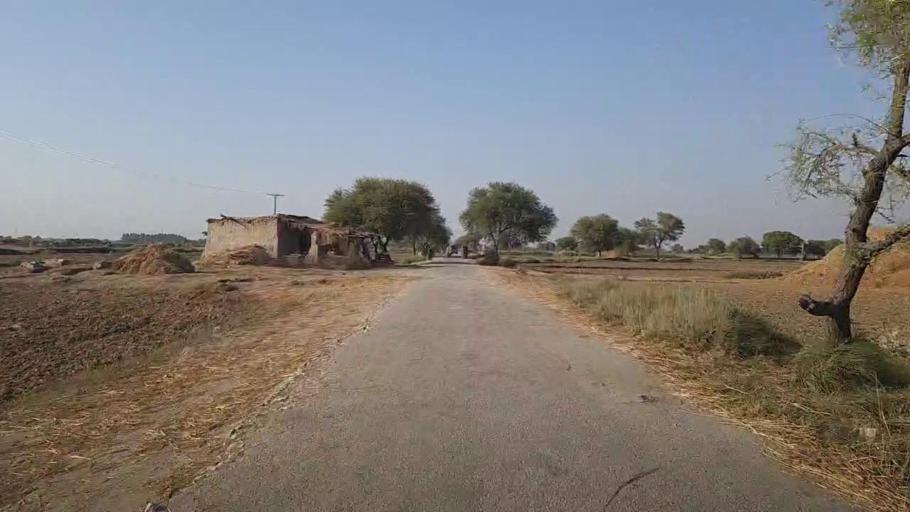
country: PK
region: Sindh
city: Kashmor
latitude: 28.4154
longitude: 69.4107
